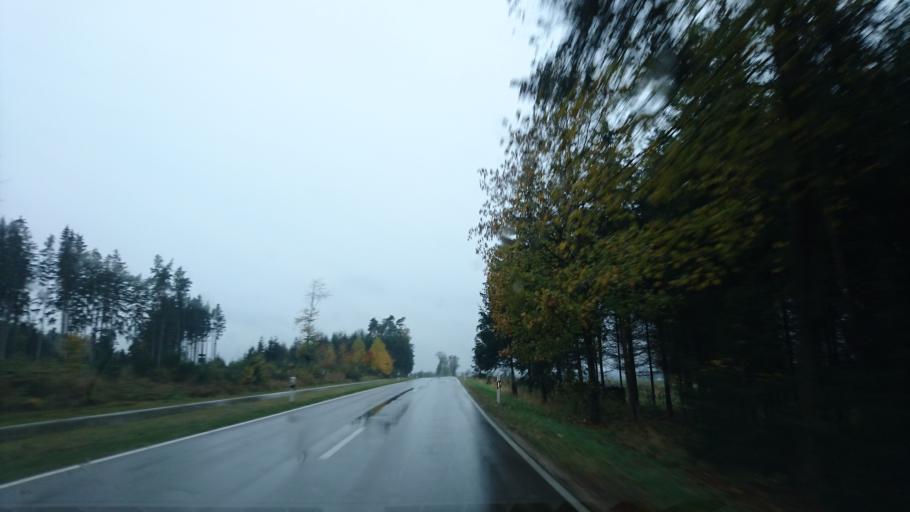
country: DE
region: Bavaria
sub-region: Swabia
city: Aichach
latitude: 48.4538
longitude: 11.1727
